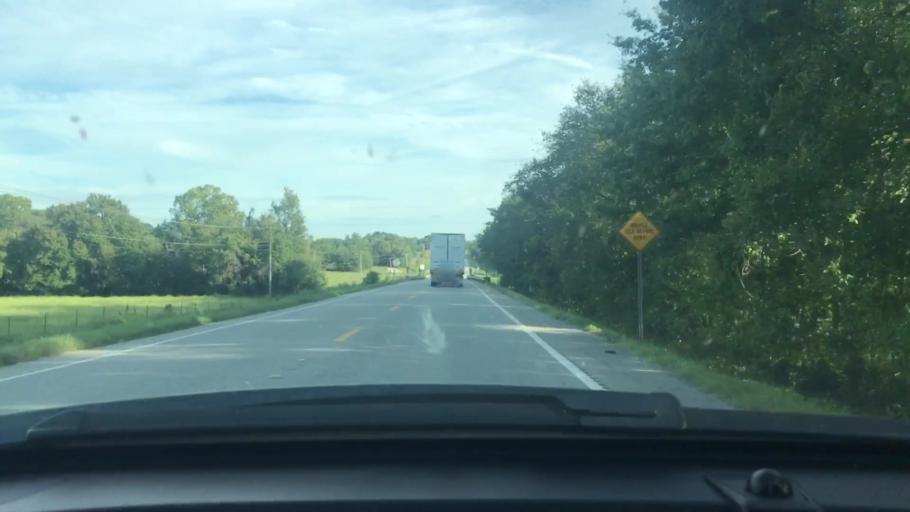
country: US
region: Arkansas
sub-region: Randolph County
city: Pocahontas
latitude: 36.1946
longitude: -91.1669
